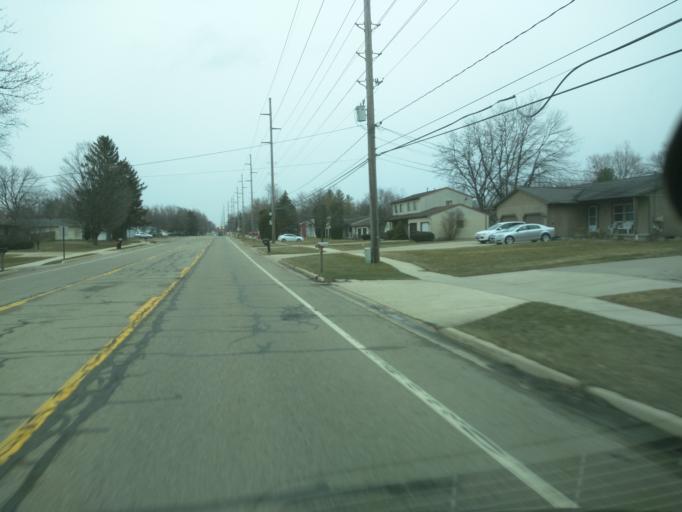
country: US
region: Michigan
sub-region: Eaton County
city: Waverly
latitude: 42.7555
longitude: -84.6274
